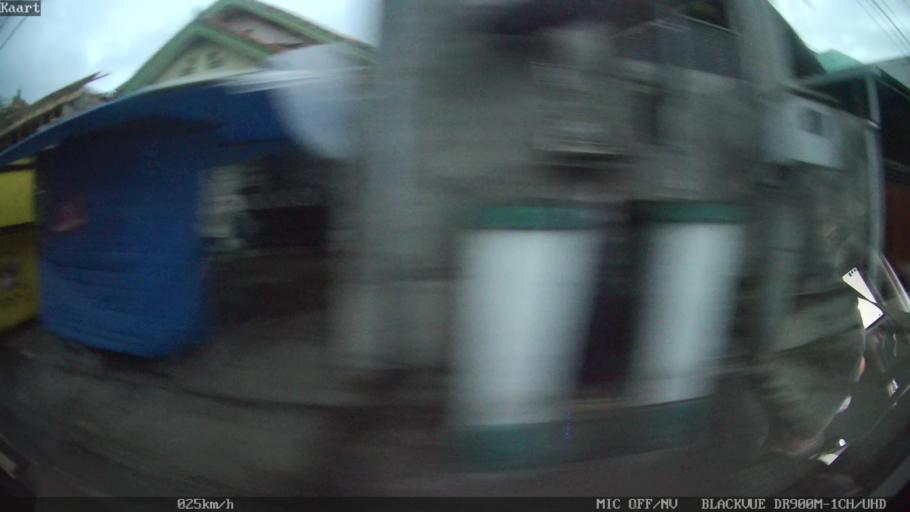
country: ID
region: Bali
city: Banjar Kertajiwa
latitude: -8.6259
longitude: 115.2682
